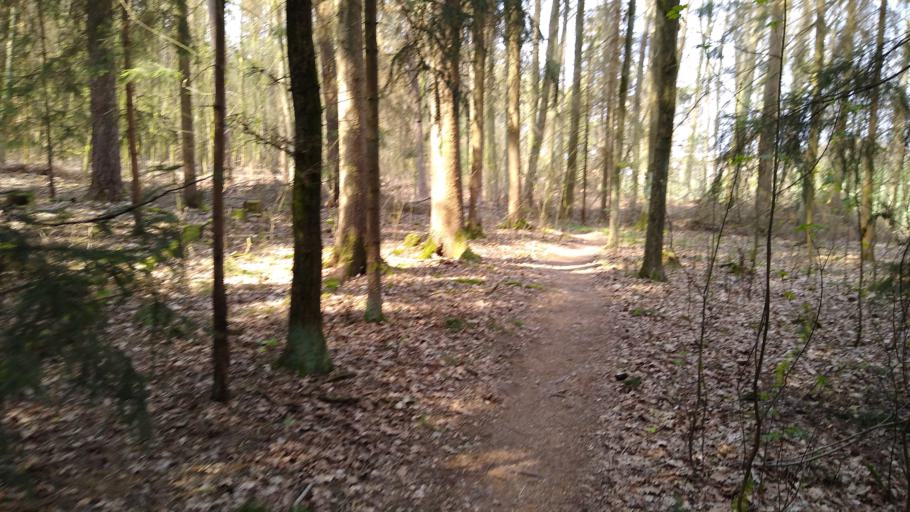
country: DE
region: Bavaria
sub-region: Regierungsbezirk Mittelfranken
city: Obermichelbach
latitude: 49.5062
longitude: 10.9137
